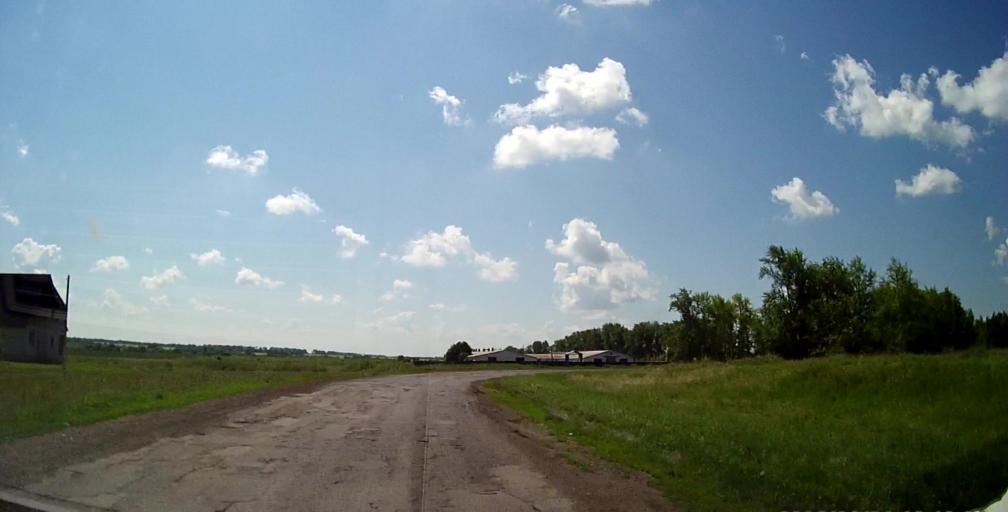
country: RU
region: Lipetsk
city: Chaplygin
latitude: 53.3168
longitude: 39.9598
